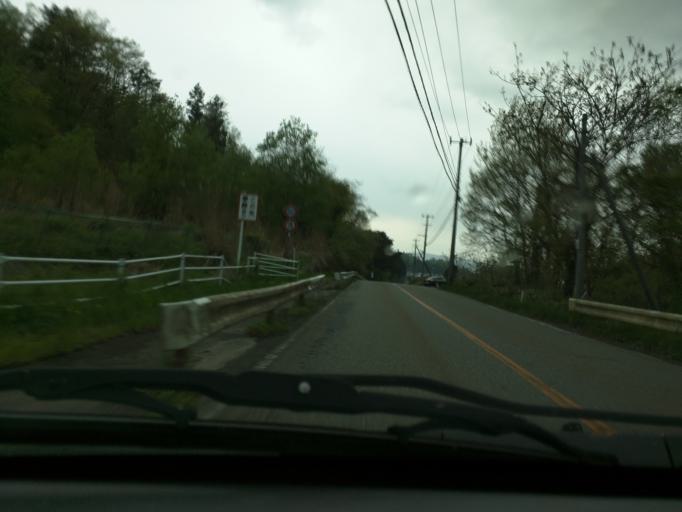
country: JP
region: Fukushima
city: Kitakata
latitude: 37.4231
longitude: 139.8951
